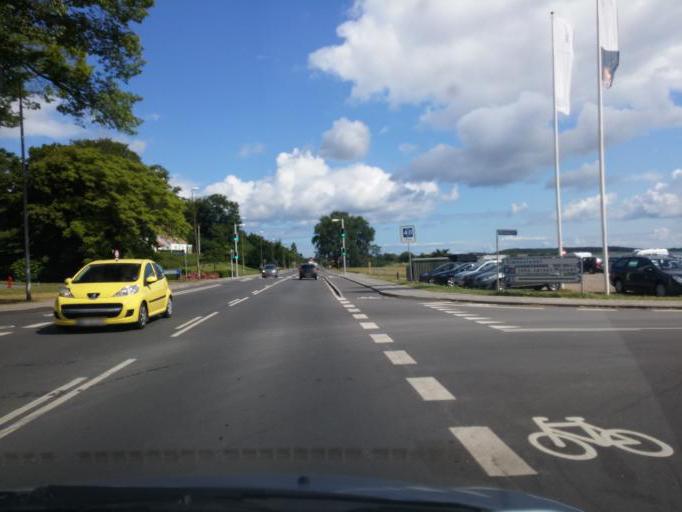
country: DK
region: South Denmark
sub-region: Kerteminde Kommune
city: Kerteminde
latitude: 55.4544
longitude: 10.6618
